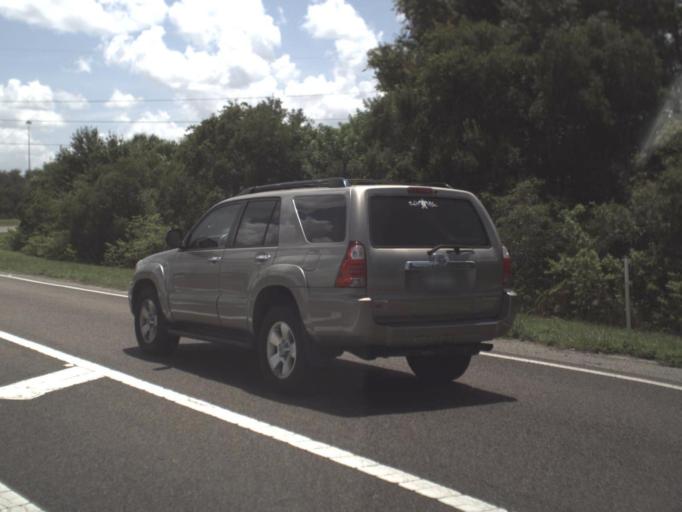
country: US
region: Florida
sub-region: Hillsborough County
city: Apollo Beach
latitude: 27.7918
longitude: -82.3613
